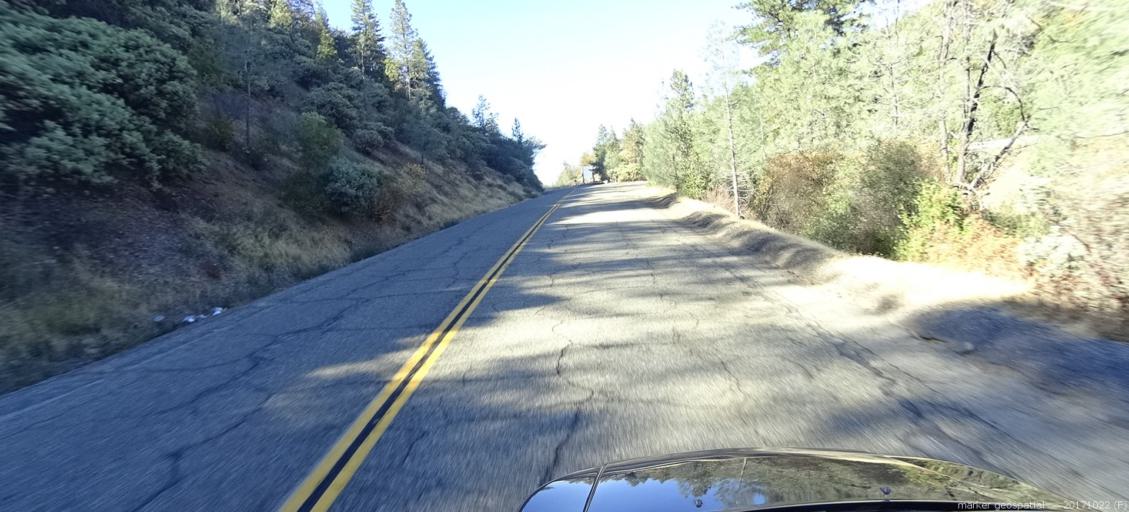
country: US
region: California
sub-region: Shasta County
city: Shasta Lake
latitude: 40.8638
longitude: -122.3617
